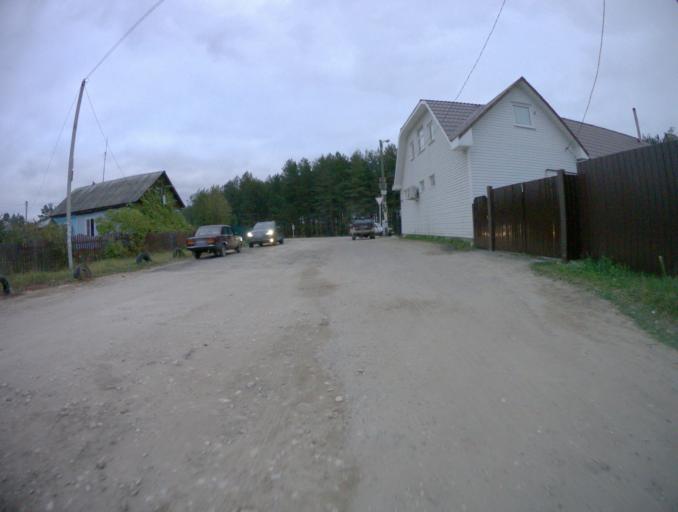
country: RU
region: Vladimir
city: Raduzhnyy
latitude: 56.0277
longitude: 40.3913
